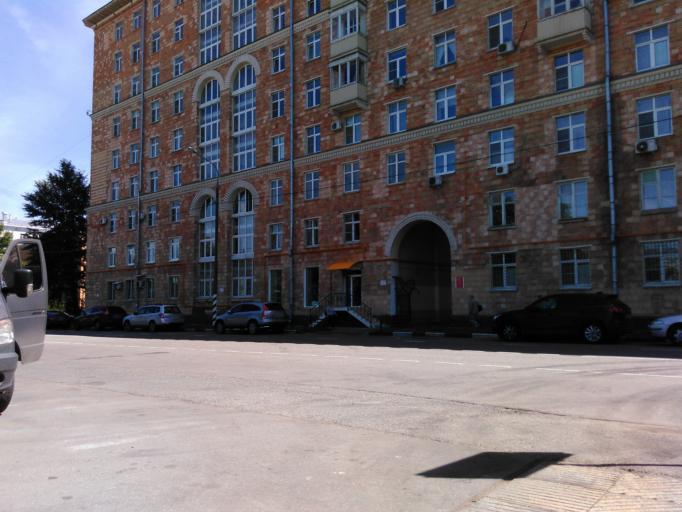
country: RU
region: Moskovskaya
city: Semenovskoye
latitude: 55.6933
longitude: 37.5404
